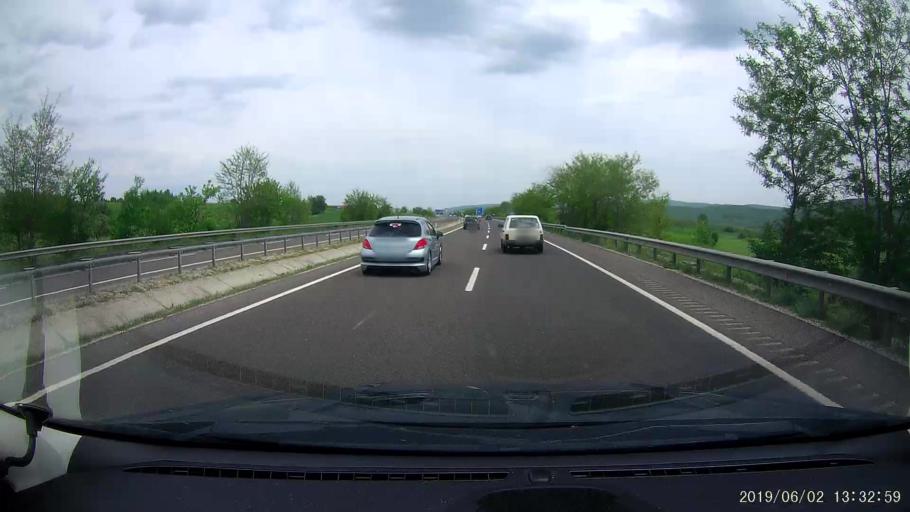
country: TR
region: Cankiri
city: Atkaracalar
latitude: 40.8004
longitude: 33.0004
